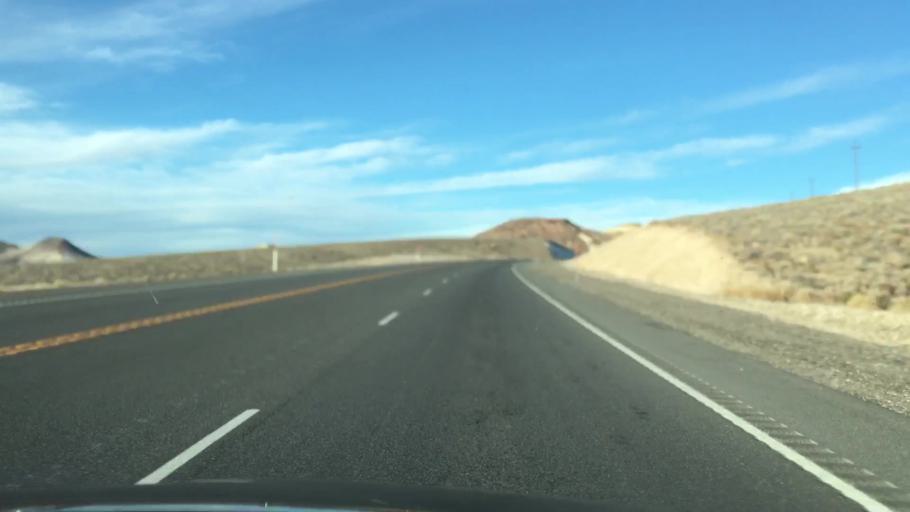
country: US
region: Nevada
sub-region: Nye County
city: Tonopah
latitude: 37.9898
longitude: -117.2733
